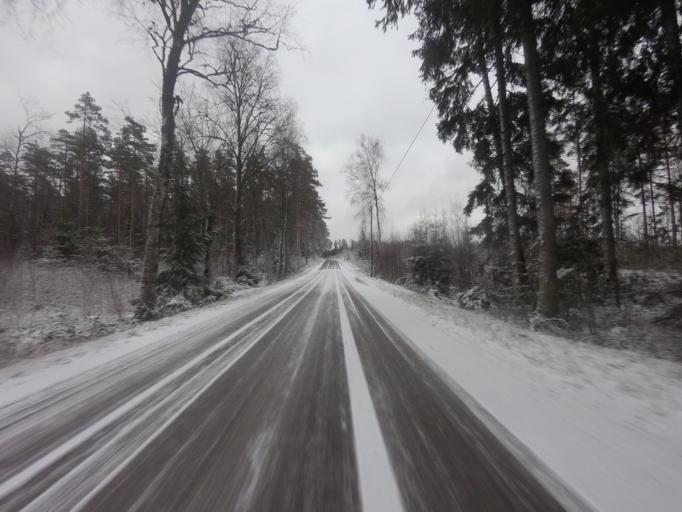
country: SE
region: Skane
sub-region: Osby Kommun
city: Lonsboda
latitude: 56.3925
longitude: 14.2679
